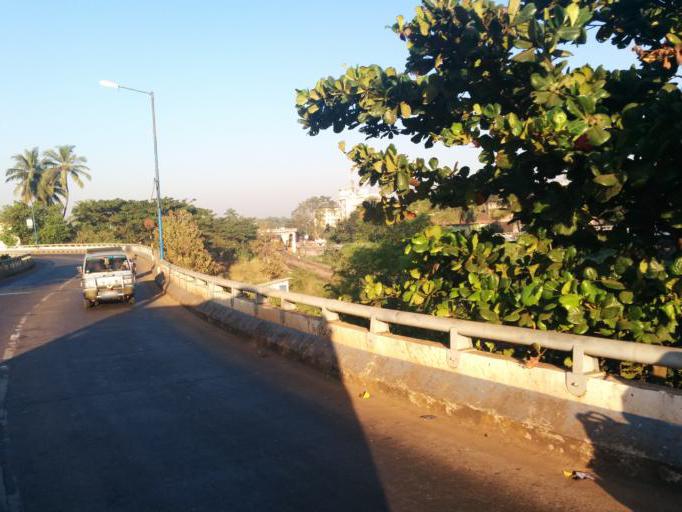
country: IN
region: Goa
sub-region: South Goa
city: Madgaon
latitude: 15.2687
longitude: 73.9607
